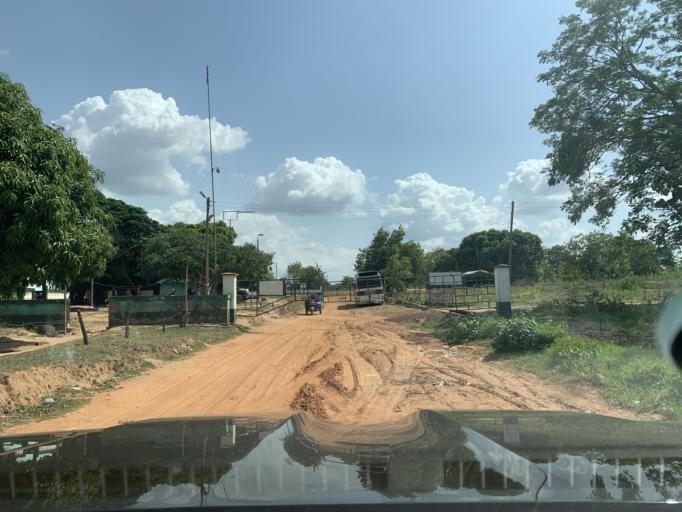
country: TG
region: Kara
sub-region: Prefecture de Bassar
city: Bassar
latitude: 9.3812
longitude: 0.5590
